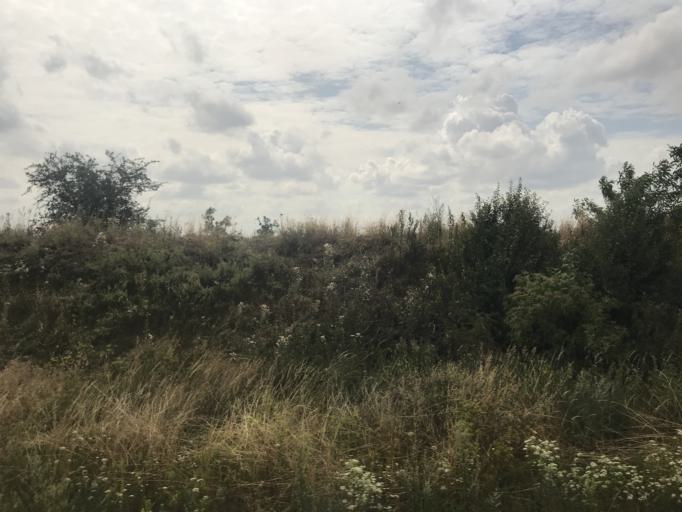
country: PL
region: Greater Poland Voivodeship
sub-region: Powiat gnieznienski
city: Gniezno
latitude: 52.5172
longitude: 17.5413
